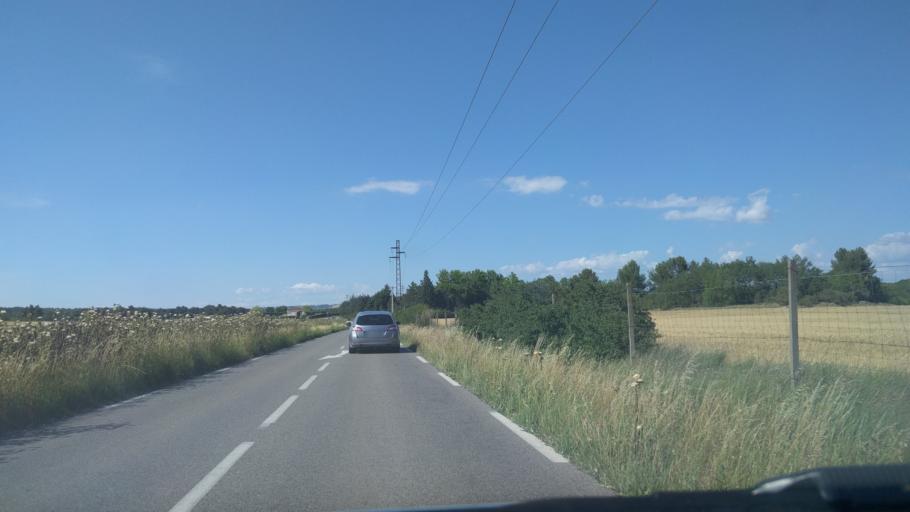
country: FR
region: Provence-Alpes-Cote d'Azur
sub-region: Departement des Bouches-du-Rhone
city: Eguilles
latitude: 43.5084
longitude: 5.3498
